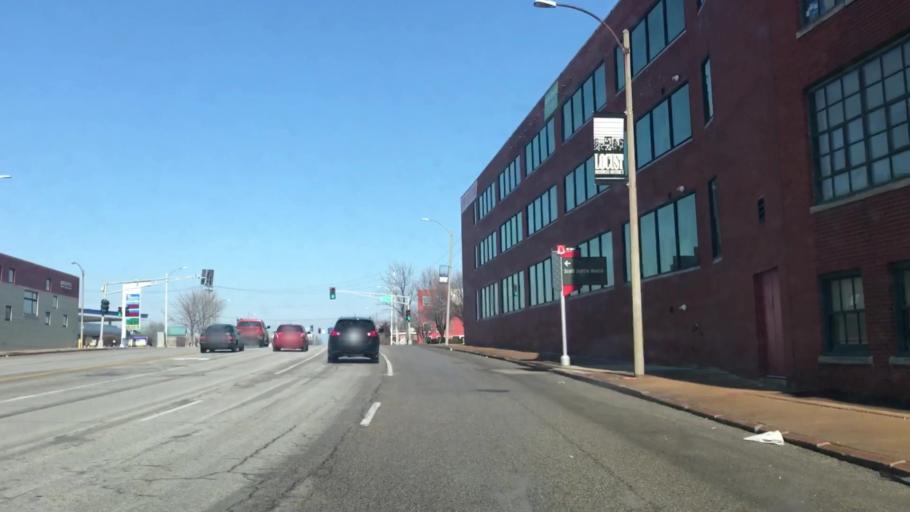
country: US
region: Missouri
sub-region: City of Saint Louis
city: St. Louis
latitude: 38.6361
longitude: -90.2127
